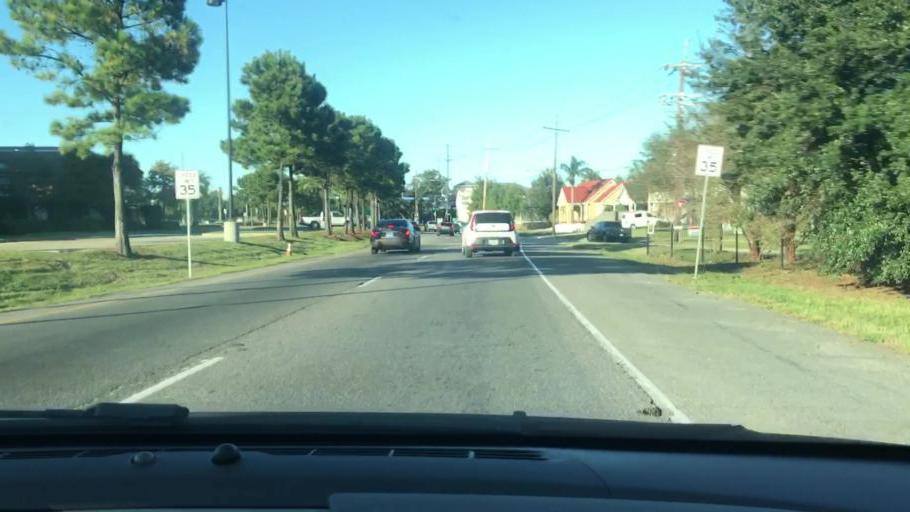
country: US
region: Louisiana
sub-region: Jefferson Parish
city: Metairie
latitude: 29.9986
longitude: -90.1154
